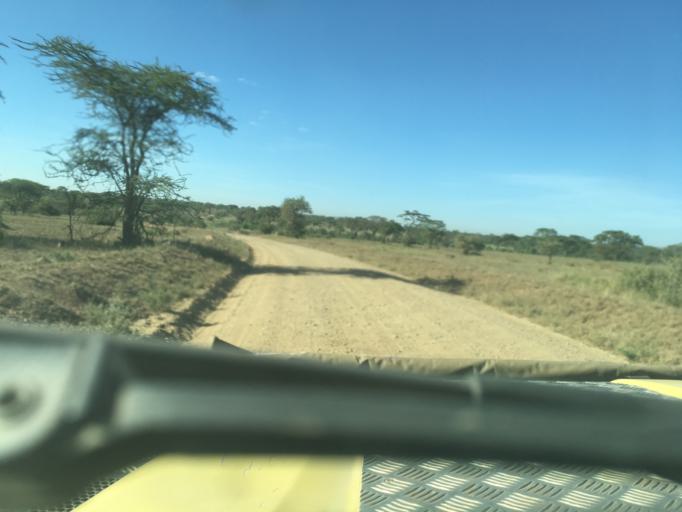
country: TZ
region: Mara
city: Mugumu
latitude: -2.3971
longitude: 34.8112
